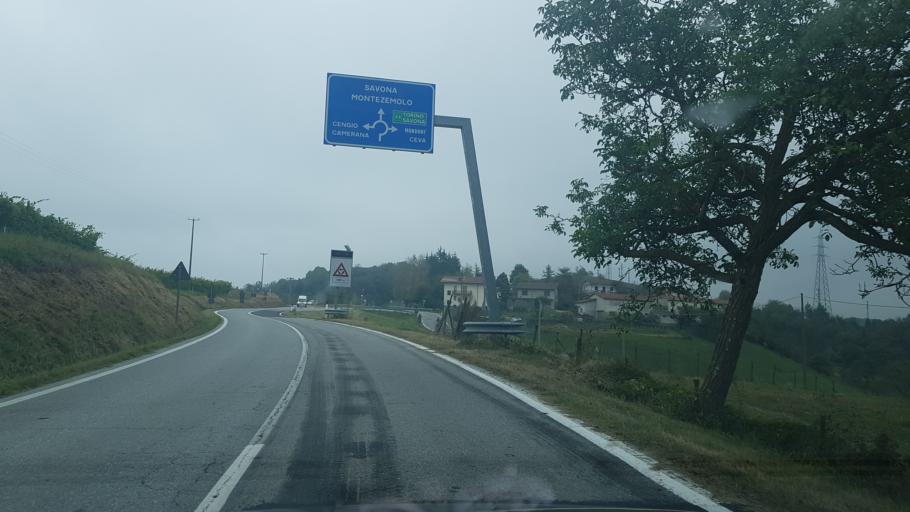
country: IT
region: Piedmont
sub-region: Provincia di Cuneo
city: Camerana
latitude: 44.4029
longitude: 8.1157
